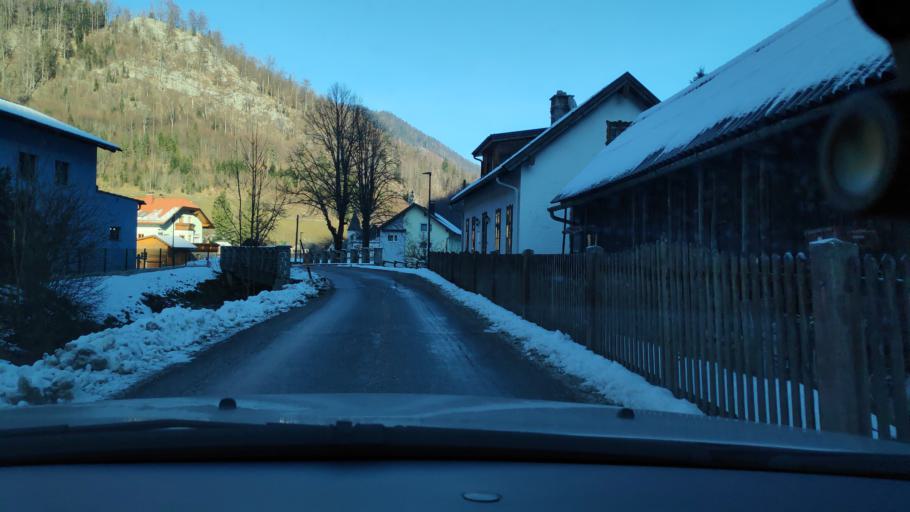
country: AT
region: Lower Austria
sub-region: Politischer Bezirk Neunkirchen
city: Schwarzau im Gebirge
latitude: 47.7617
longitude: 15.6945
